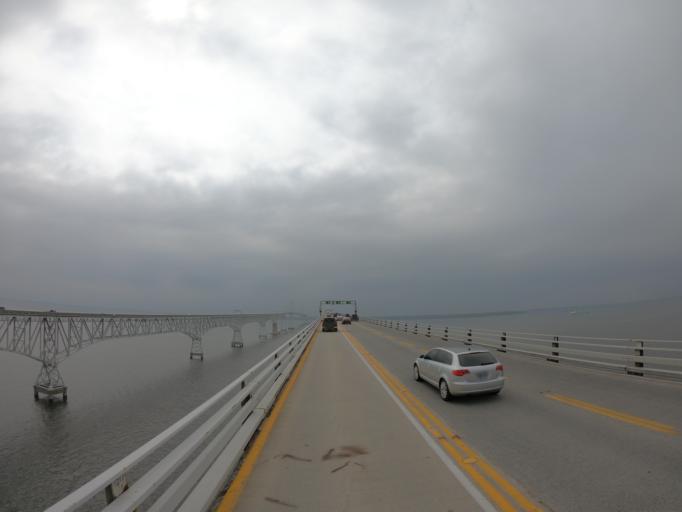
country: US
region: Maryland
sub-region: Queen Anne's County
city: Stevensville
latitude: 38.9908
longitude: -76.3666
